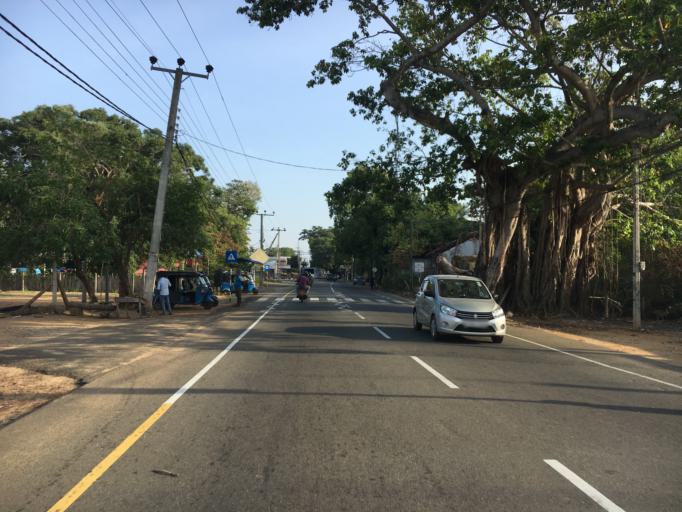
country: LK
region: Eastern Province
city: Eravur Town
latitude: 7.9069
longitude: 81.5341
